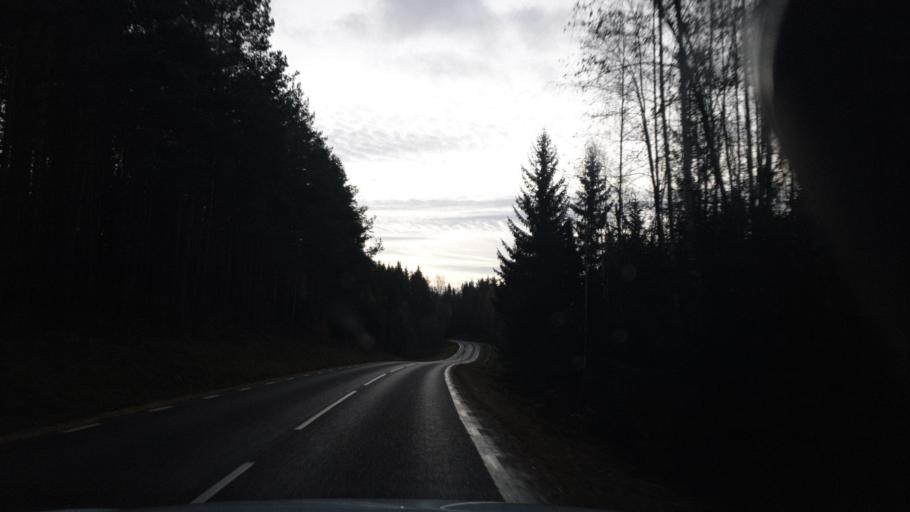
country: SE
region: Vaermland
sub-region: Arvika Kommun
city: Arvika
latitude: 59.6267
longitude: 12.8573
